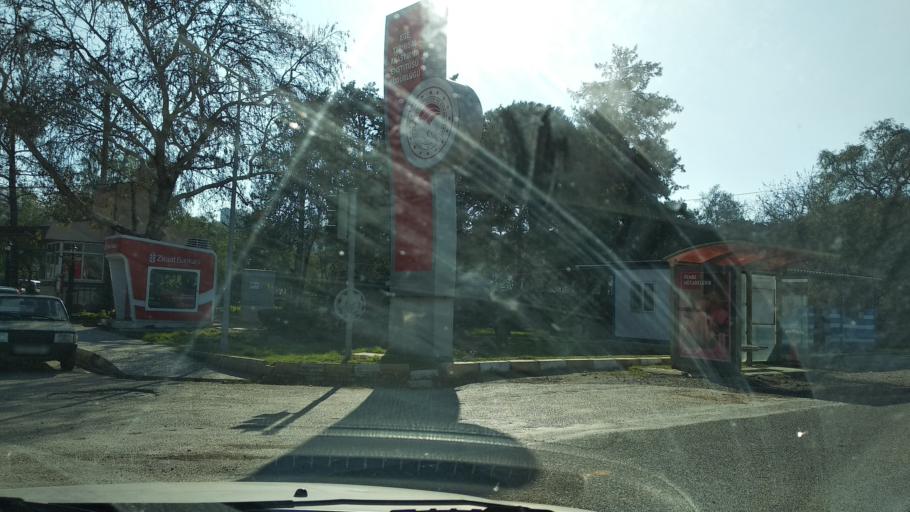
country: TR
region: Izmir
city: Menemen
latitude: 38.5667
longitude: 27.0521
